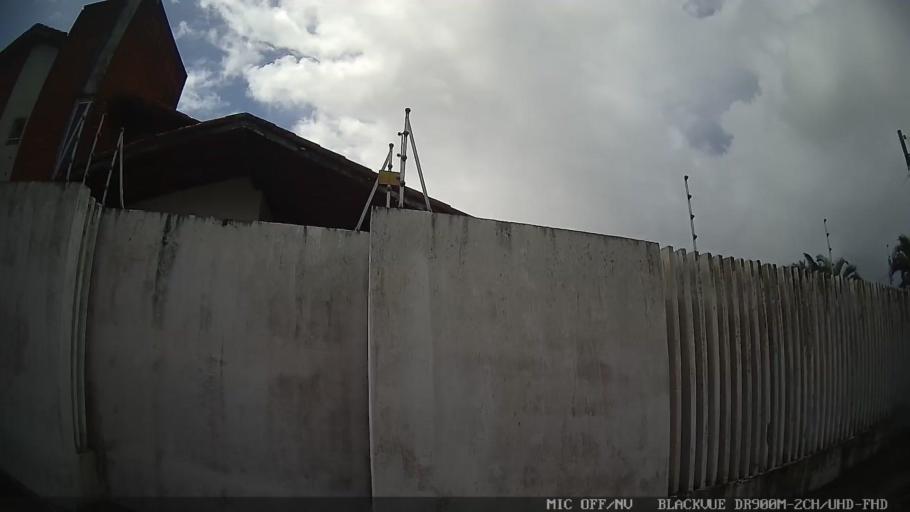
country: BR
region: Sao Paulo
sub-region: Itanhaem
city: Itanhaem
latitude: -24.1966
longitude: -46.8069
